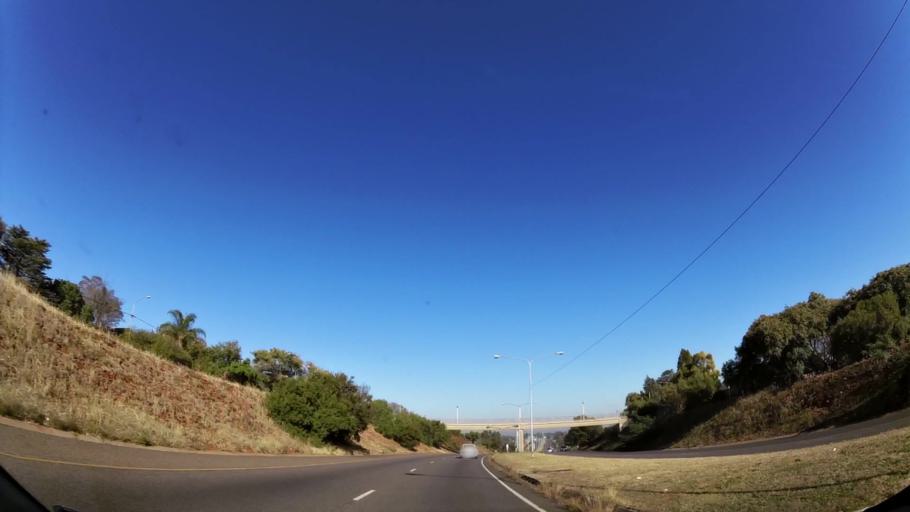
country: ZA
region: Gauteng
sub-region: City of Tshwane Metropolitan Municipality
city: Centurion
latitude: -25.8160
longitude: 28.2081
